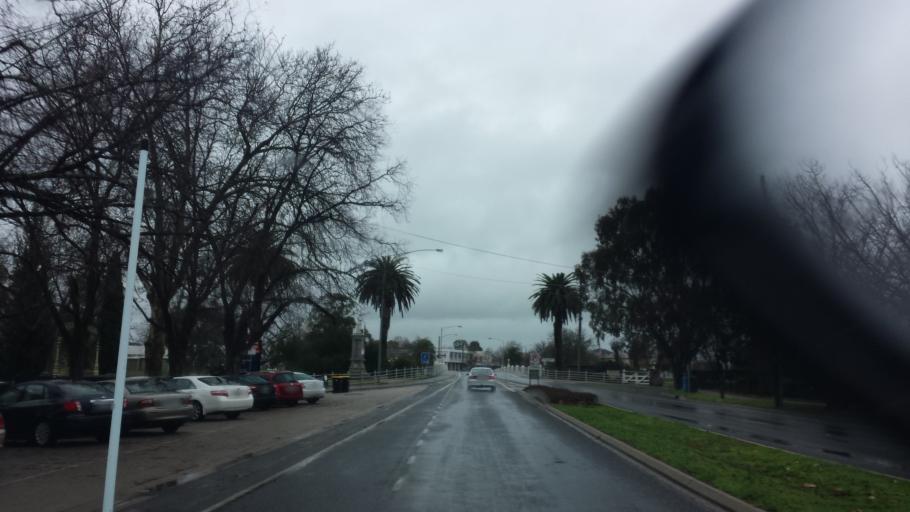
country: AU
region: Victoria
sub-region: Benalla
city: Benalla
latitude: -36.5533
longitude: 145.9795
